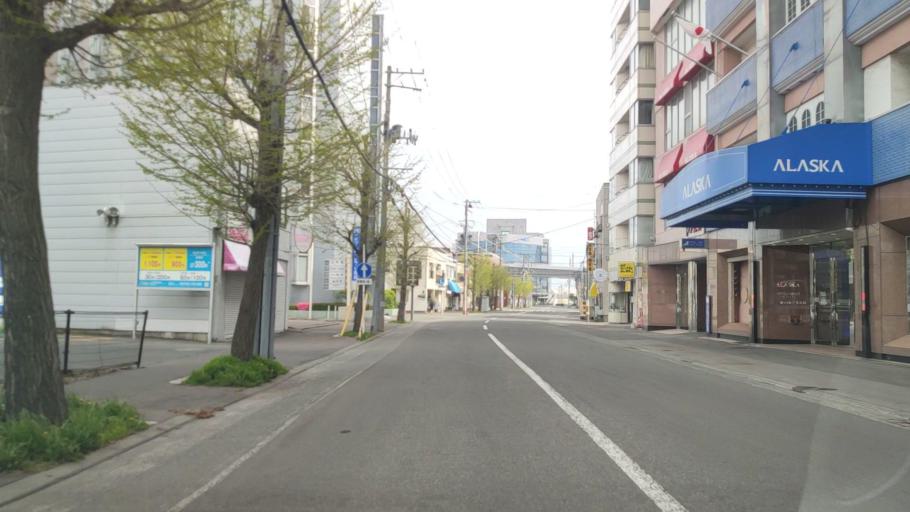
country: JP
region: Aomori
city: Aomori Shi
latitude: 40.8271
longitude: 140.7384
